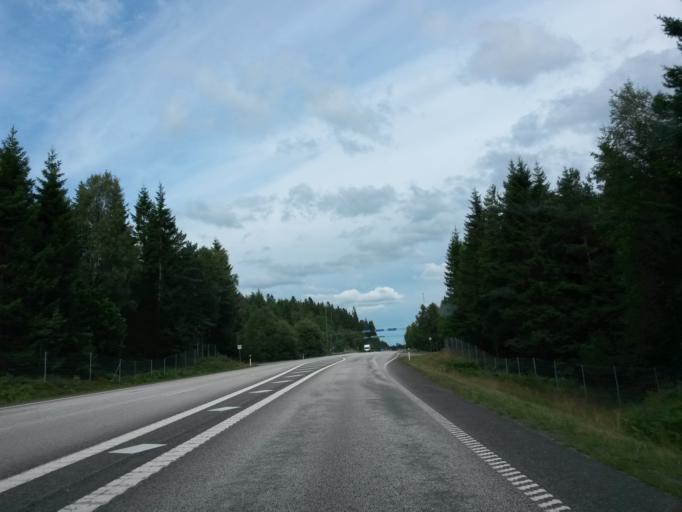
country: SE
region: Vaestra Goetaland
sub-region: Marks Kommun
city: Fritsla
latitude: 57.5378
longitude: 12.8014
